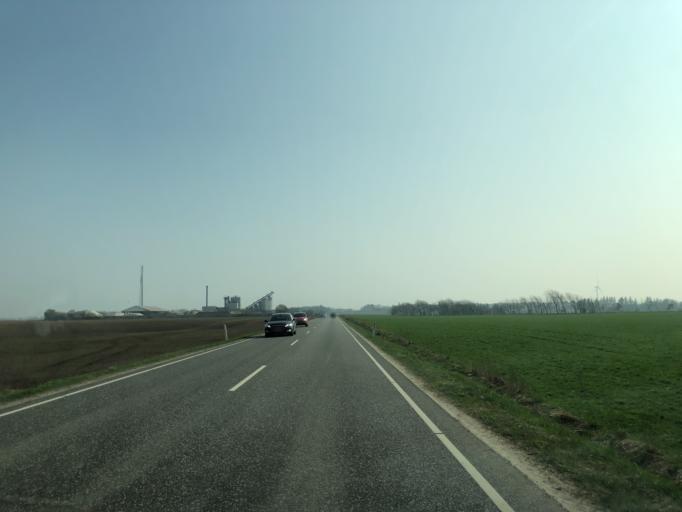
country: DK
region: Central Jutland
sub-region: Ringkobing-Skjern Kommune
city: Videbaek
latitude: 56.0961
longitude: 8.5077
